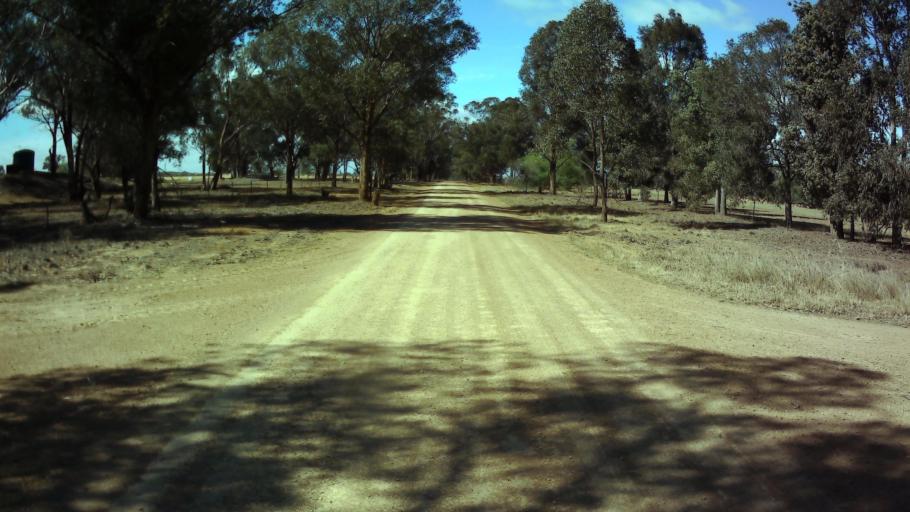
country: AU
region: New South Wales
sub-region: Weddin
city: Grenfell
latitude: -34.0449
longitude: 148.3150
